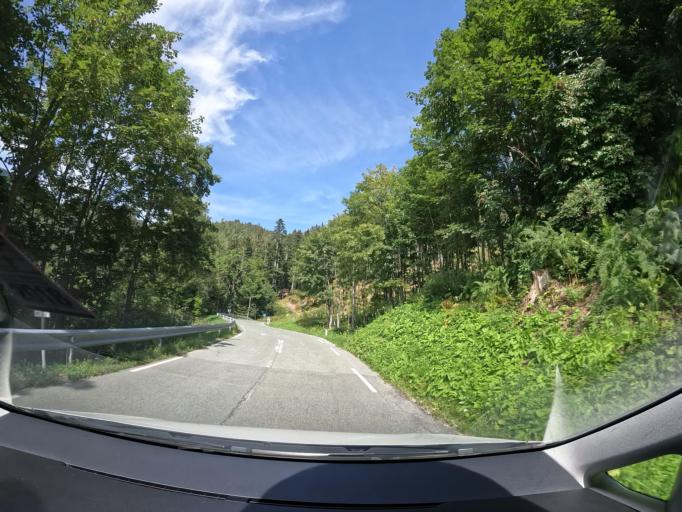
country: AT
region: Carinthia
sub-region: Politischer Bezirk Sankt Veit an der Glan
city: Liebenfels
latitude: 46.7136
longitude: 14.2584
